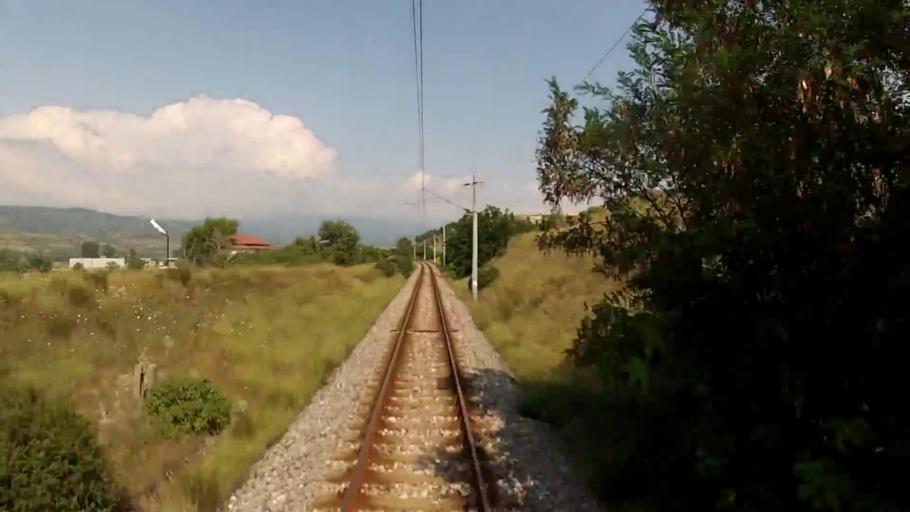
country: BG
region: Blagoevgrad
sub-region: Obshtina Strumyani
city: Strumyani
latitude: 41.6240
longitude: 23.2156
